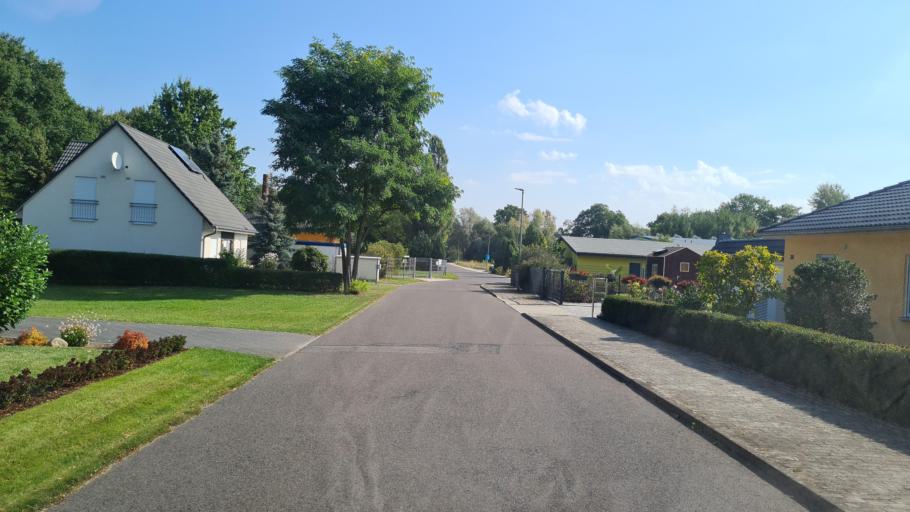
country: DE
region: Brandenburg
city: Kolkwitz
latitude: 51.7337
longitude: 14.2569
